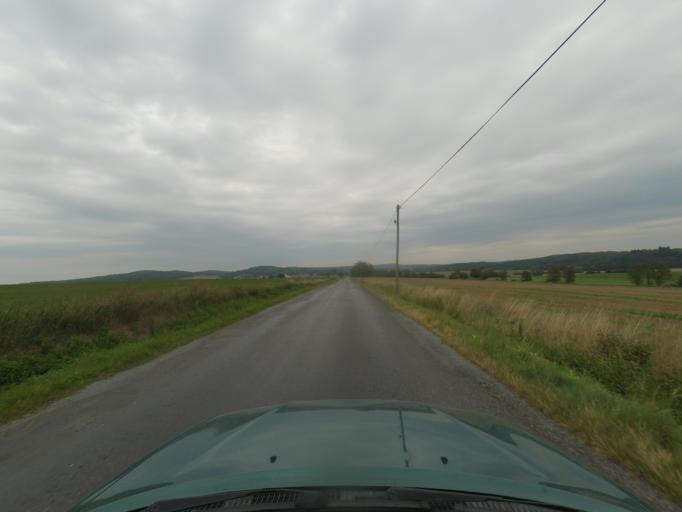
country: CZ
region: Plzensky
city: Merklin
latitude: 49.5577
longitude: 13.1737
